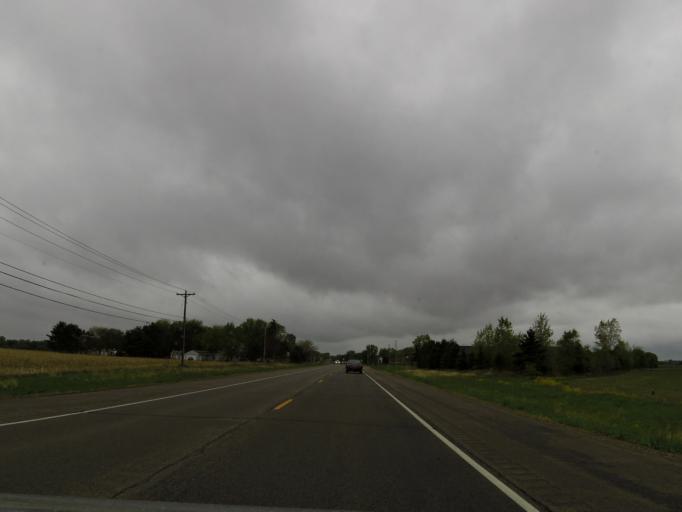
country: US
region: Minnesota
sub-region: Washington County
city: Lake Elmo
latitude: 45.0071
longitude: -92.8704
